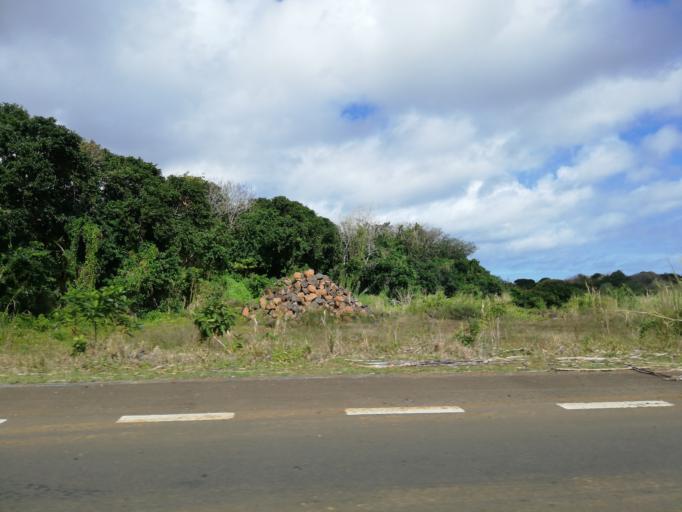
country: MU
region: Grand Port
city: Plaine Magnien
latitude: -20.4165
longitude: 57.6719
